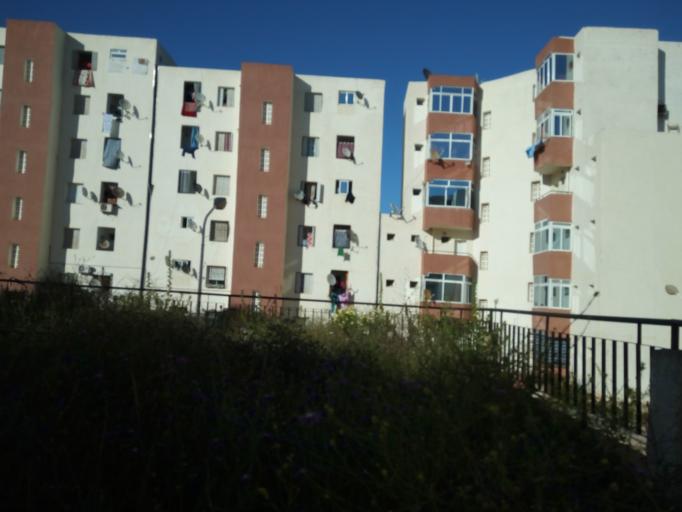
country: DZ
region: Tipaza
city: Saoula
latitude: 36.7148
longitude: 3.0155
